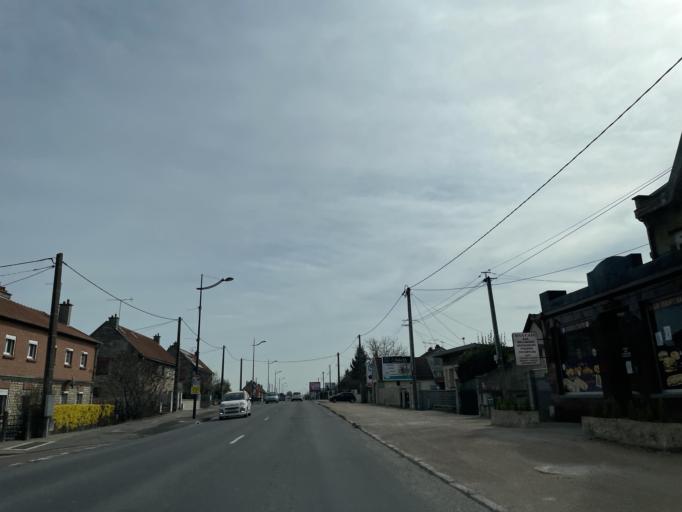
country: FR
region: Champagne-Ardenne
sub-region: Departement de l'Aube
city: Romilly-sur-Seine
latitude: 48.5080
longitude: 3.7404
